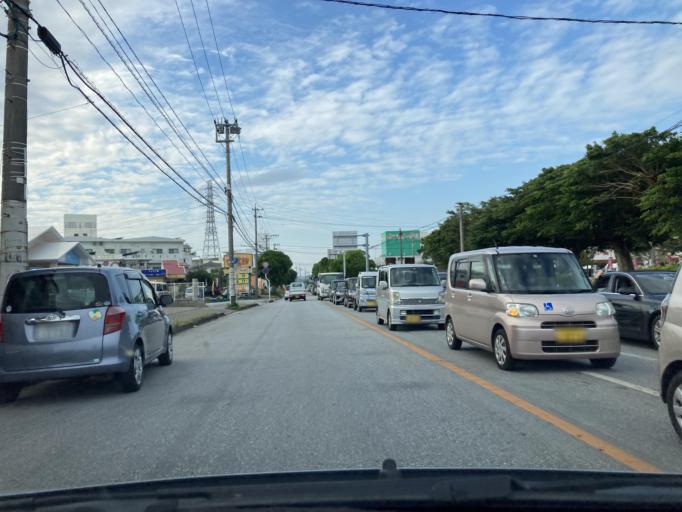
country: JP
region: Okinawa
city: Okinawa
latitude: 26.3672
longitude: 127.8169
